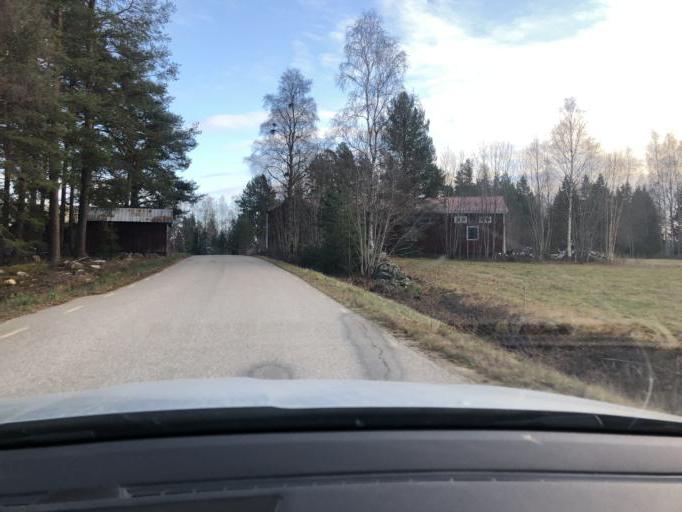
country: SE
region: Gaevleborg
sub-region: Hudiksvalls Kommun
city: Sorforsa
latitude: 61.7130
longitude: 16.9375
